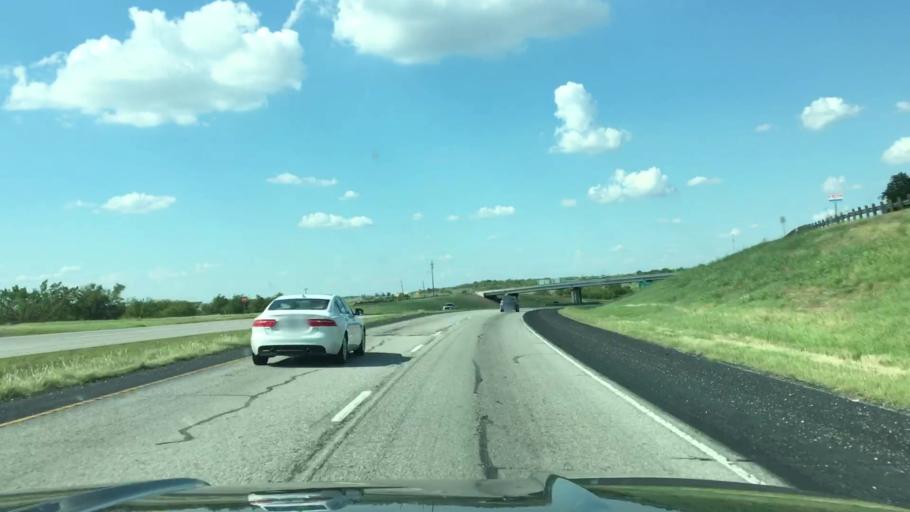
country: US
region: Texas
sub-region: Wise County
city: Rhome
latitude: 33.0531
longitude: -97.4788
